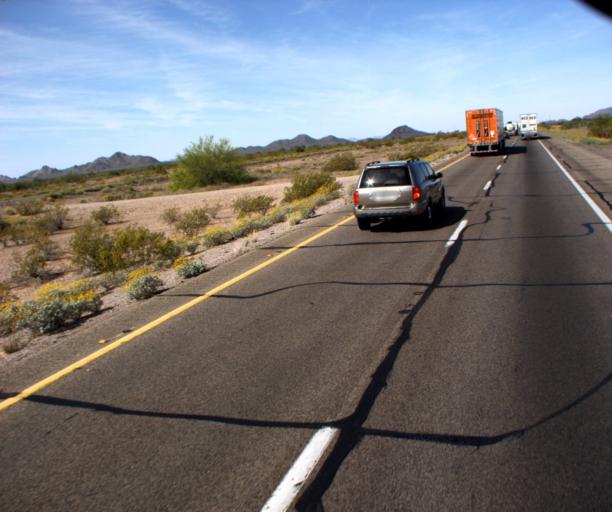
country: US
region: Arizona
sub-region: Maricopa County
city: Buckeye
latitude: 33.5026
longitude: -112.9621
